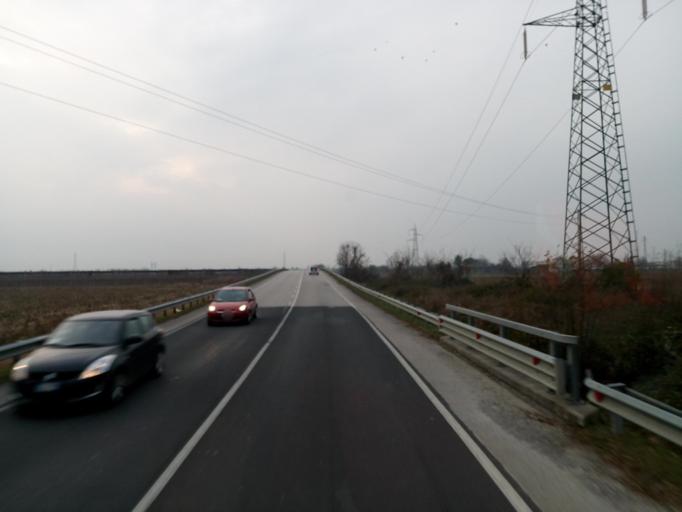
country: IT
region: Friuli Venezia Giulia
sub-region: Provincia di Udine
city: Reana del Rojale
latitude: 46.1196
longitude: 13.2599
